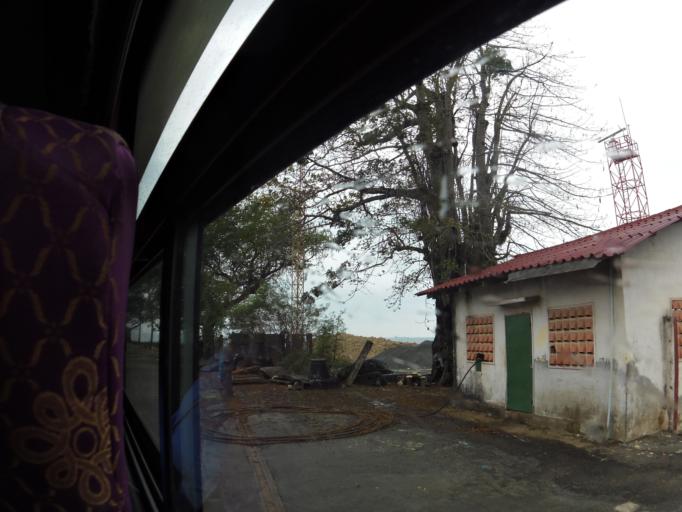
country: KH
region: Preah Sihanouk
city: Sihanoukville
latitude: 10.6456
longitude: 103.5018
